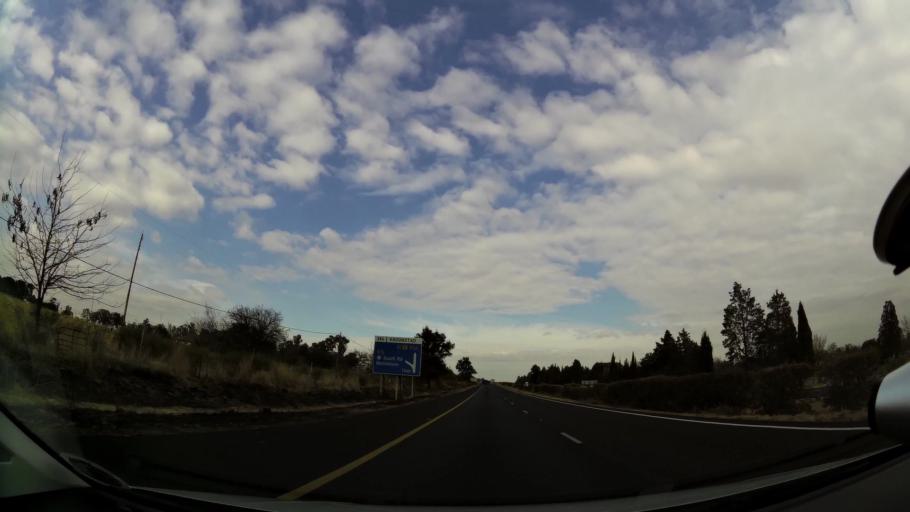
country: ZA
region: Orange Free State
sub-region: Fezile Dabi District Municipality
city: Kroonstad
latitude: -27.6770
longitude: 27.2497
